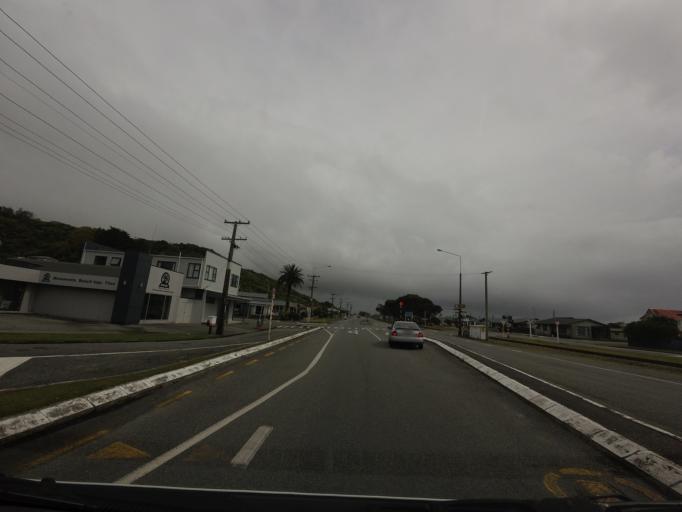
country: NZ
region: West Coast
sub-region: Grey District
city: Greymouth
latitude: -42.4661
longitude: 171.1923
